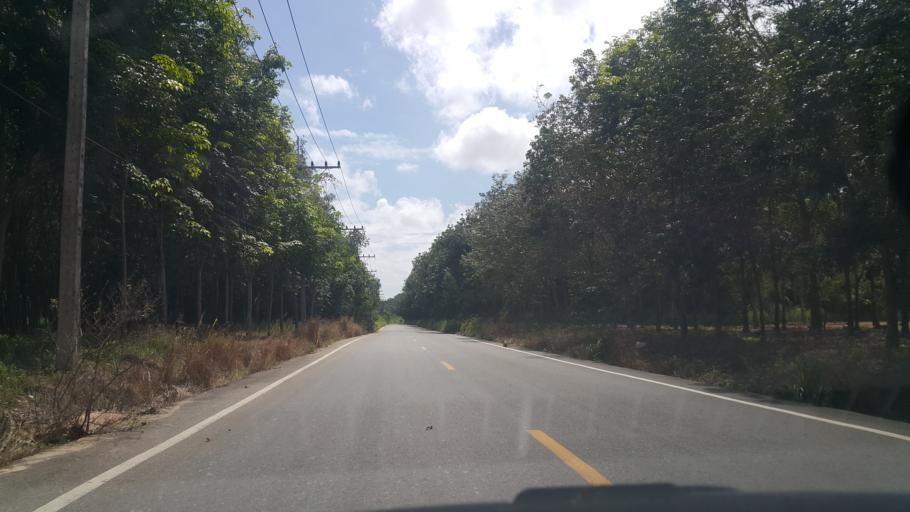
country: TH
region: Rayong
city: Ban Chang
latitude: 12.8091
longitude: 101.0002
